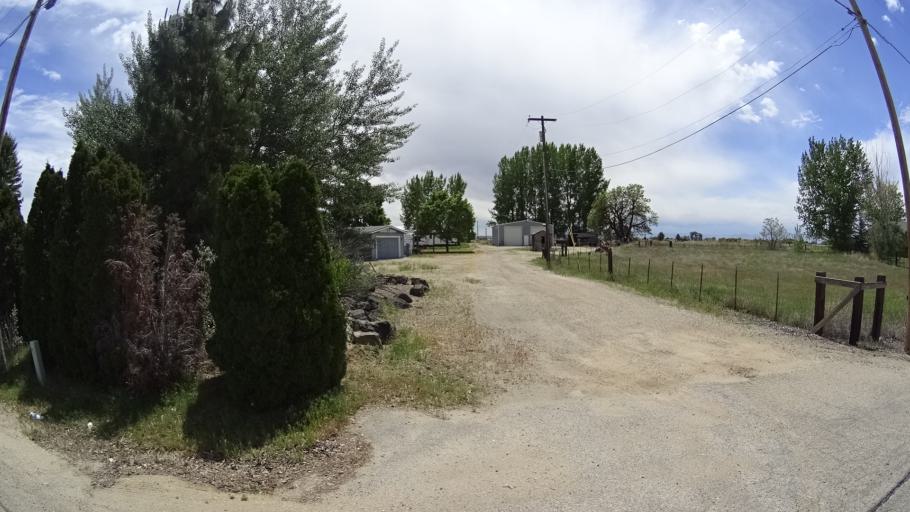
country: US
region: Idaho
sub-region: Ada County
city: Meridian
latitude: 43.5757
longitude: -116.4297
